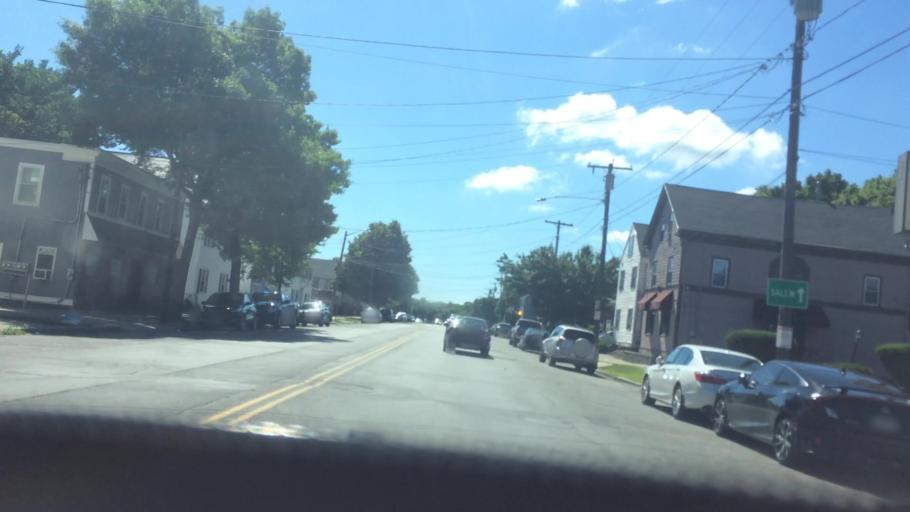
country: US
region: Massachusetts
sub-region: Essex County
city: Peabody
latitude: 42.5214
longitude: -70.9142
